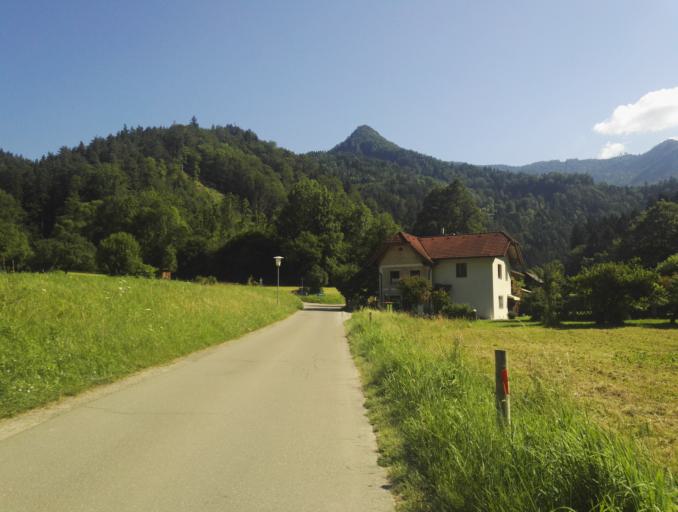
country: AT
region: Styria
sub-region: Politischer Bezirk Graz-Umgebung
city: Rothelstein
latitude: 47.3326
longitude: 15.3680
